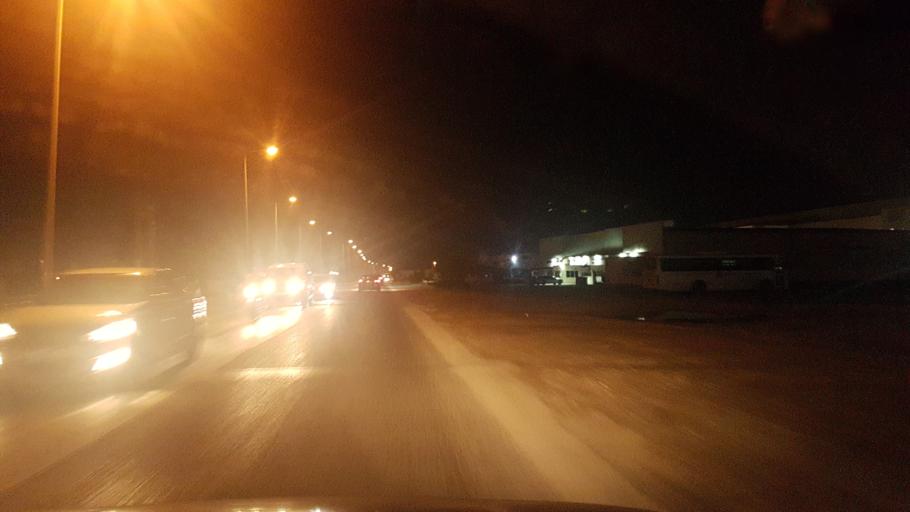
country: BH
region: Muharraq
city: Al Hadd
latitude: 26.2743
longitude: 50.6435
